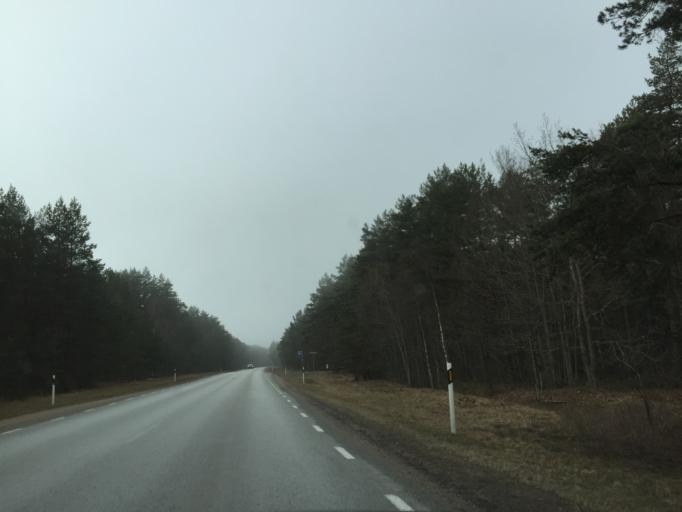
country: EE
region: Saare
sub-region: Kuressaare linn
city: Kuressaare
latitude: 58.1986
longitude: 22.2835
